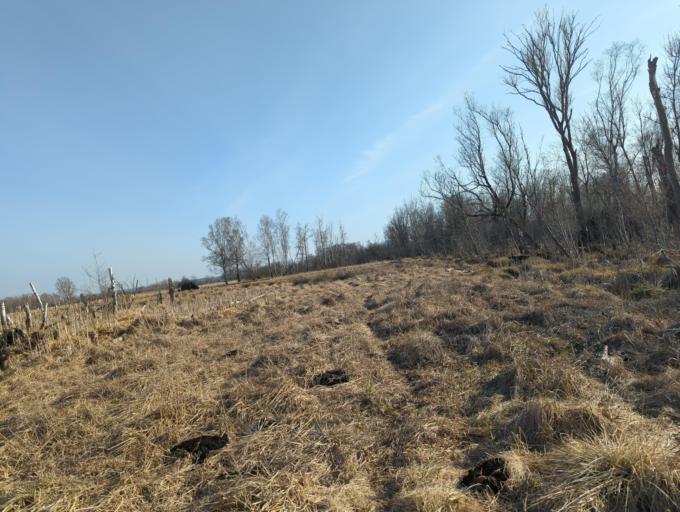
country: DE
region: Bavaria
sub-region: Swabia
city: Leipheim
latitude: 48.4822
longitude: 10.2032
